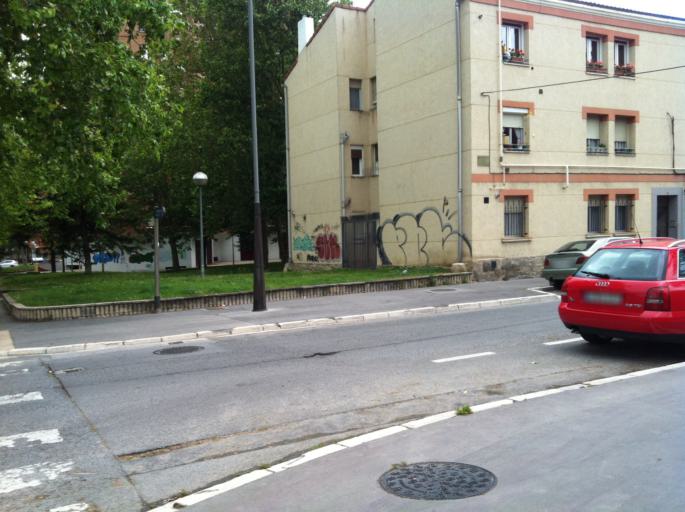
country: ES
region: Basque Country
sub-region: Provincia de Alava
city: Gasteiz / Vitoria
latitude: 42.8347
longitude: -2.6663
